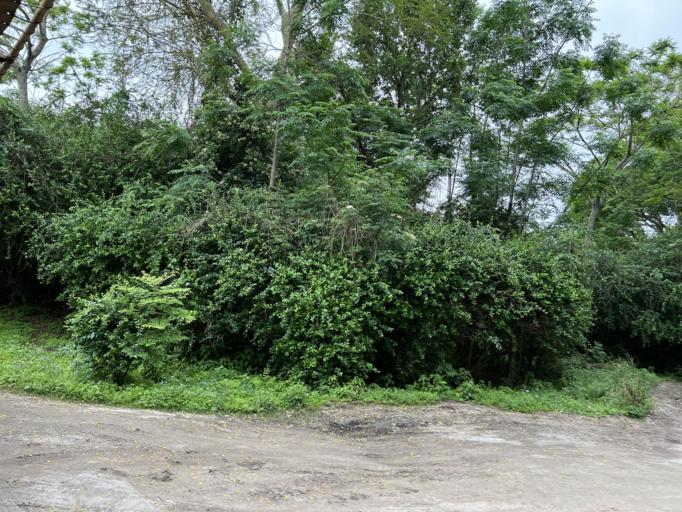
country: US
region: Florida
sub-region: Polk County
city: Citrus Ridge
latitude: 28.3642
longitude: -81.5925
